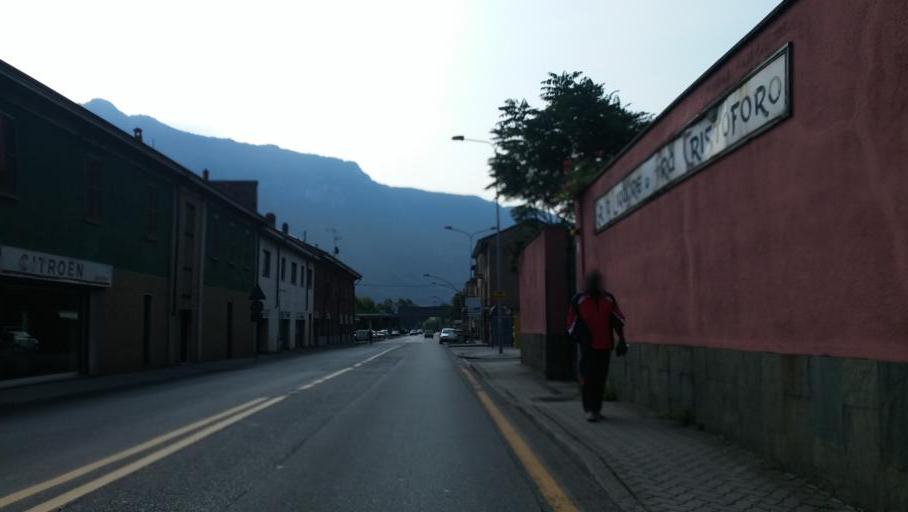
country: IT
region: Lombardy
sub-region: Provincia di Lecco
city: Lecco
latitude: 45.8467
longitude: 9.3923
